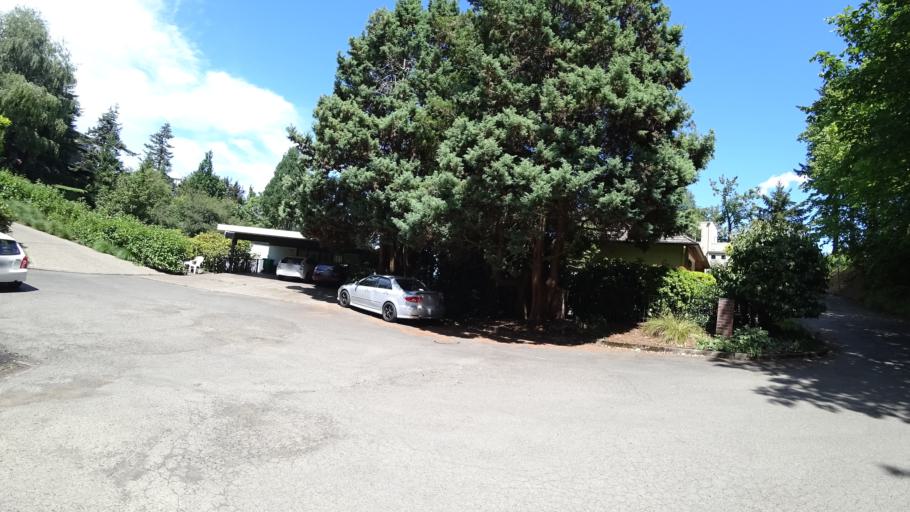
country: US
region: Oregon
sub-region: Multnomah County
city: Portland
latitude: 45.5064
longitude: -122.6896
